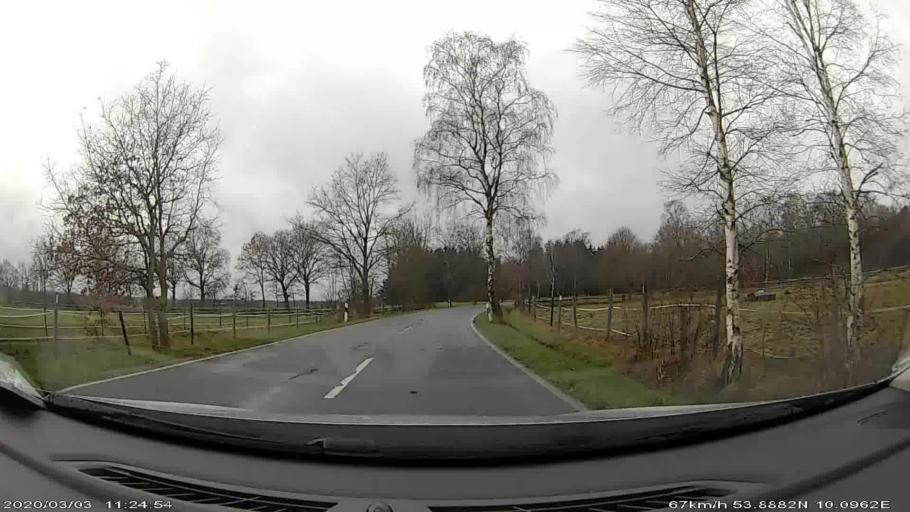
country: DE
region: Schleswig-Holstein
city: Hartenholm
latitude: 53.8892
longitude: 10.0919
